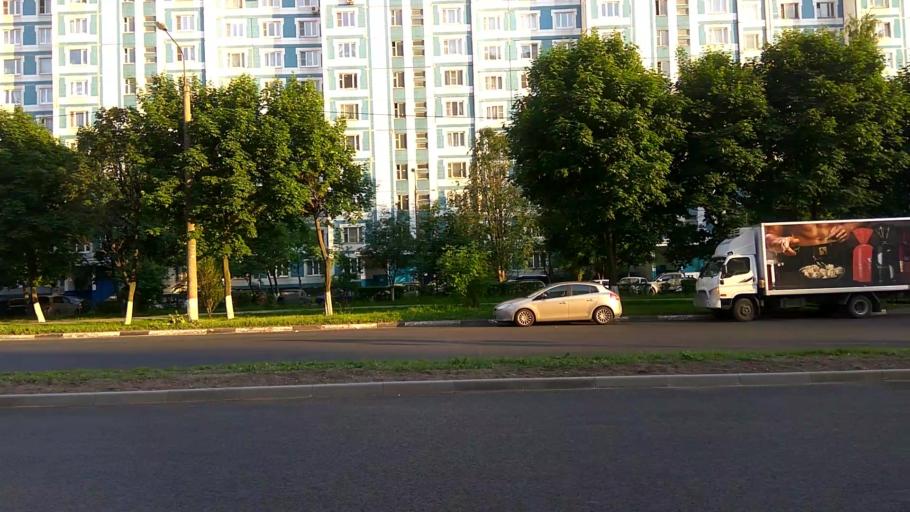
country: RU
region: Moskovskaya
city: Yubileyny
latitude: 55.9131
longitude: 37.8647
